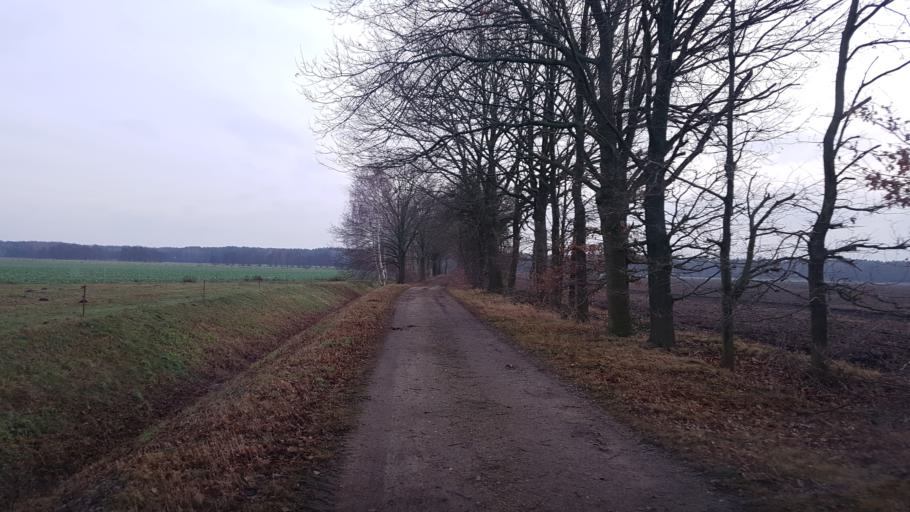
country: DE
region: Brandenburg
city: Ruckersdorf
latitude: 51.5935
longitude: 13.6139
